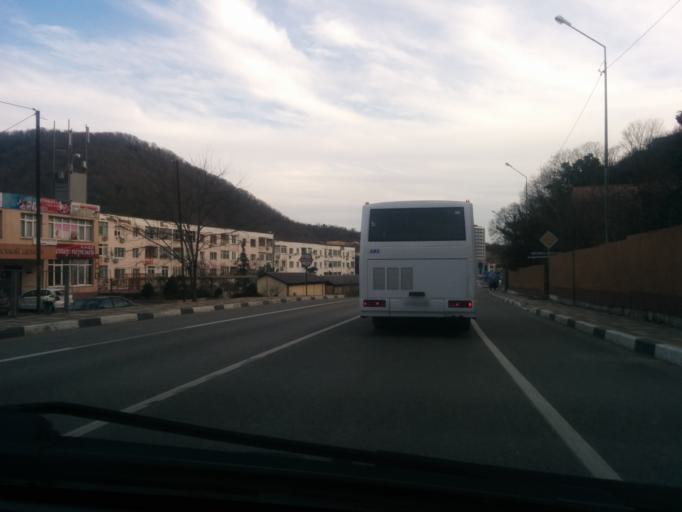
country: RU
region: Krasnodarskiy
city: Ol'ginka
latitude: 44.2018
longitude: 38.8869
